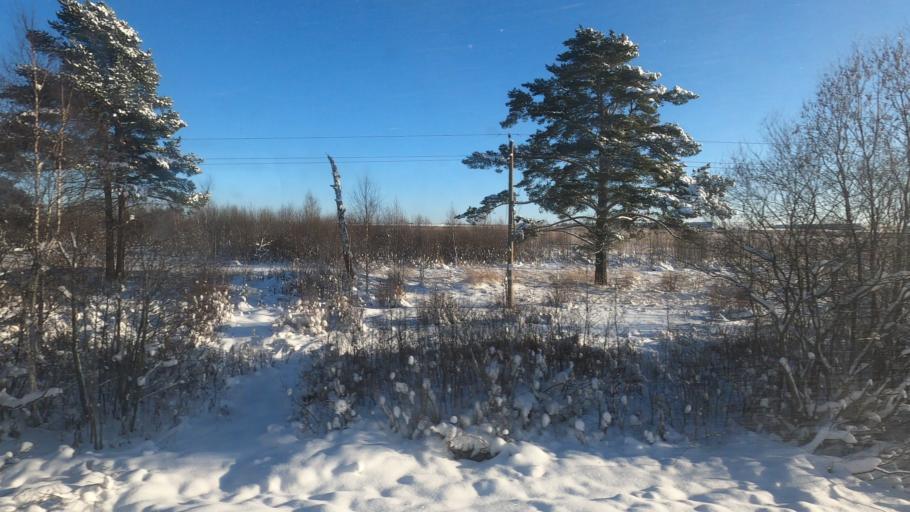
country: RU
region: Moskovskaya
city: Orud'yevo
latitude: 56.4275
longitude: 37.4987
